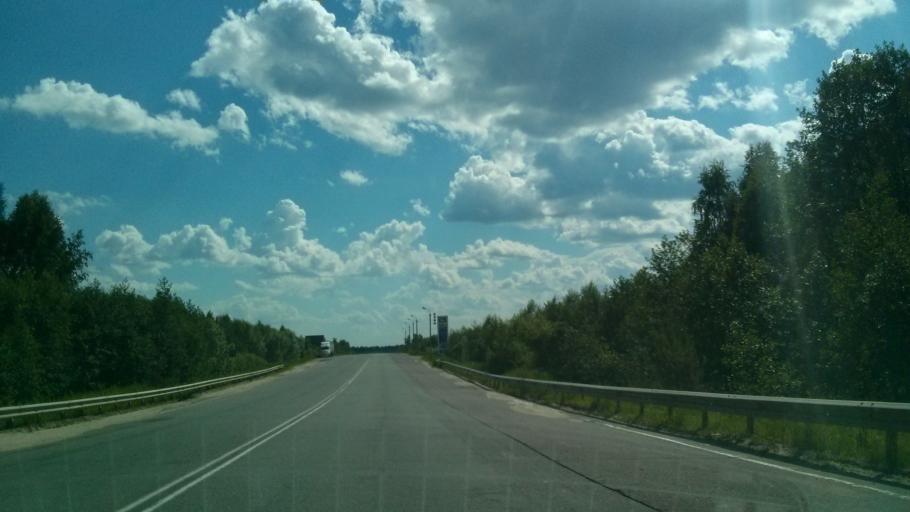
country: RU
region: Vladimir
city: Melenki
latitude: 55.3403
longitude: 41.6675
